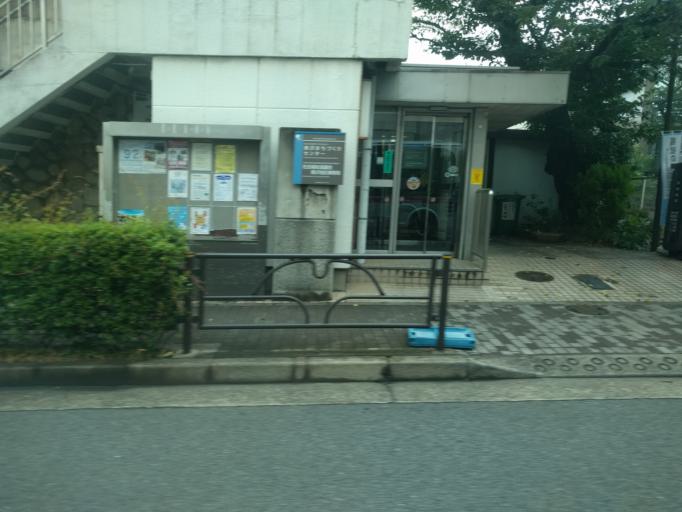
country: JP
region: Kanagawa
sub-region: Kawasaki-shi
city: Kawasaki
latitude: 35.5998
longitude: 139.6731
